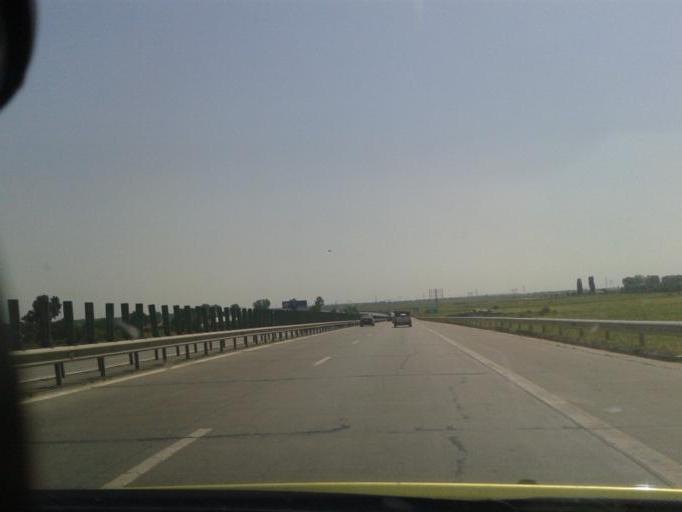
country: RO
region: Ilfov
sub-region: Comuna Cernica
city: Caldararu
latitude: 44.4086
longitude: 26.2625
